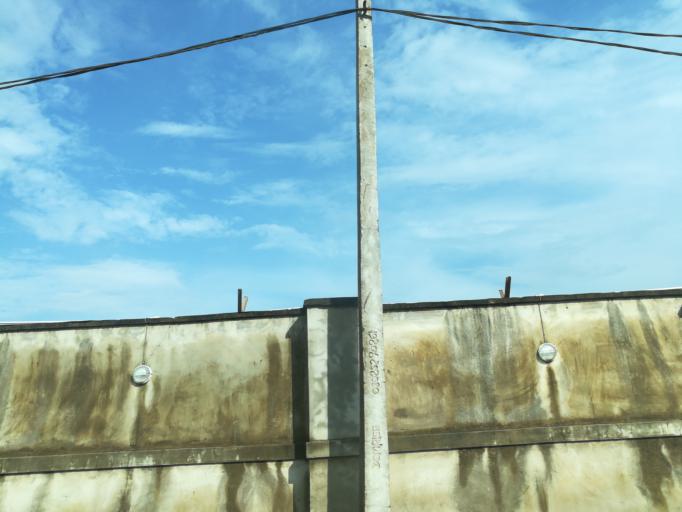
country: NG
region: Lagos
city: Ojota
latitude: 6.6016
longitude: 3.4212
